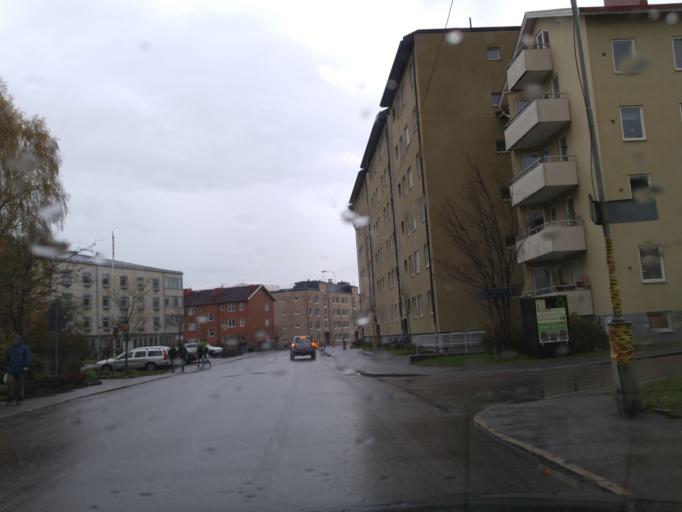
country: SE
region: Vaestra Goetaland
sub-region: Goteborg
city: Majorna
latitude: 57.6702
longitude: 11.9273
